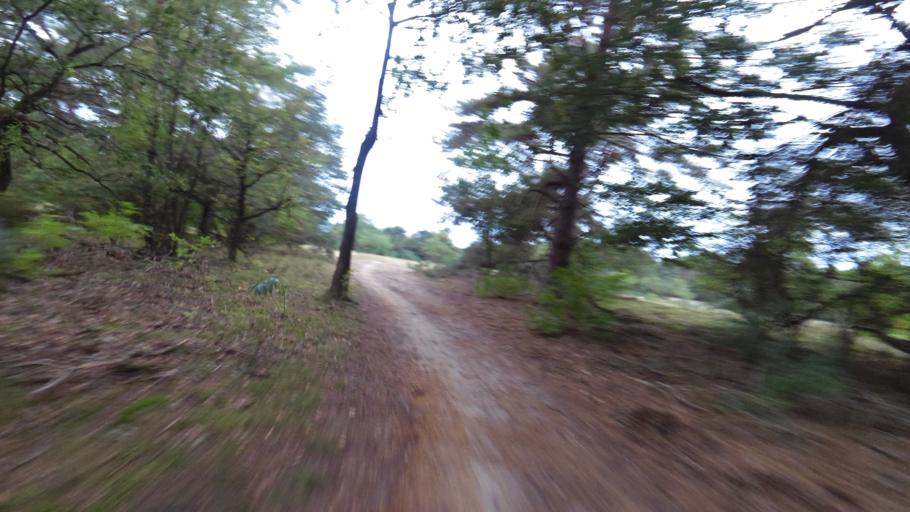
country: NL
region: Gelderland
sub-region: Gemeente Apeldoorn
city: Uddel
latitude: 52.1880
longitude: 5.8017
